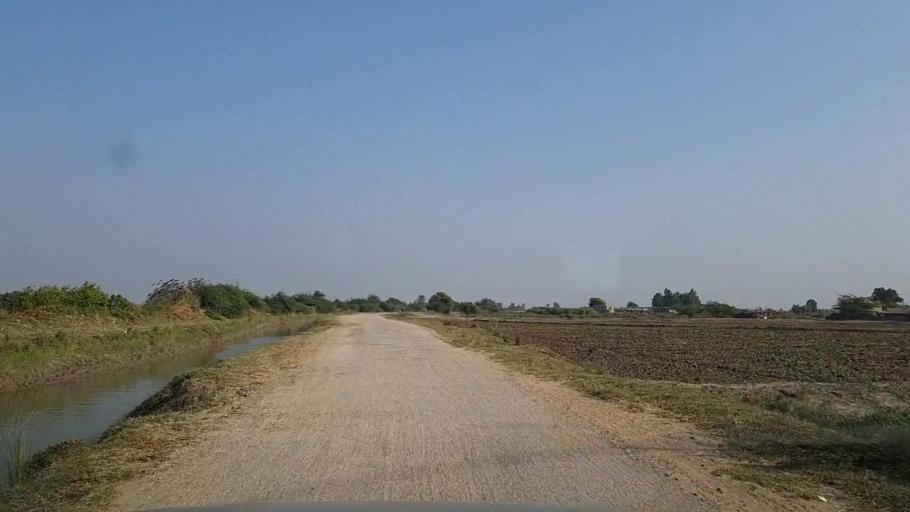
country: PK
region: Sindh
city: Mirpur Sakro
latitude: 24.5961
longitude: 67.5966
